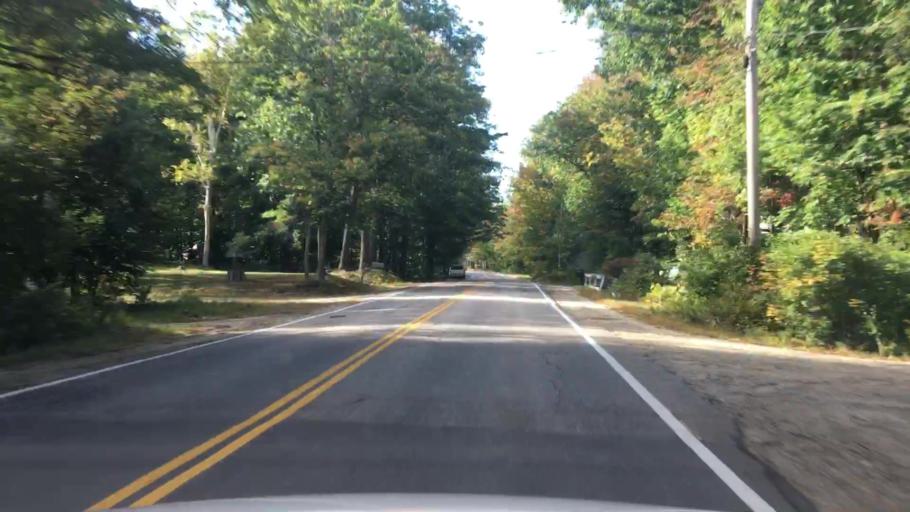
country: US
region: Maine
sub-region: Androscoggin County
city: Lisbon Falls
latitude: 43.9559
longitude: -70.0443
